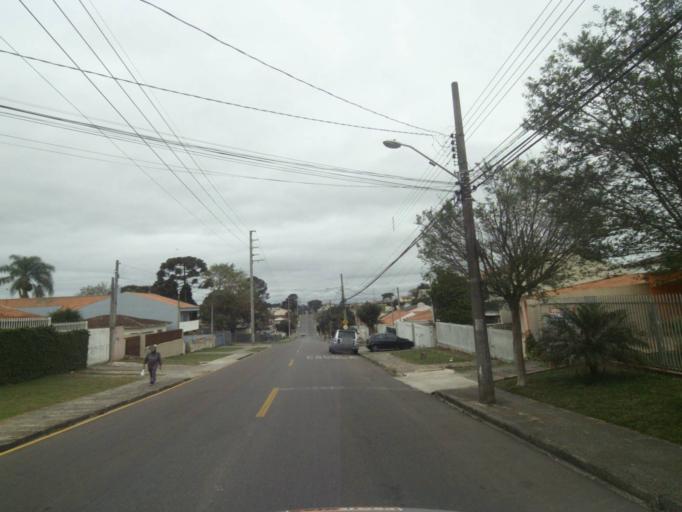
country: BR
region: Parana
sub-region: Pinhais
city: Pinhais
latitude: -25.4814
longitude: -49.2278
